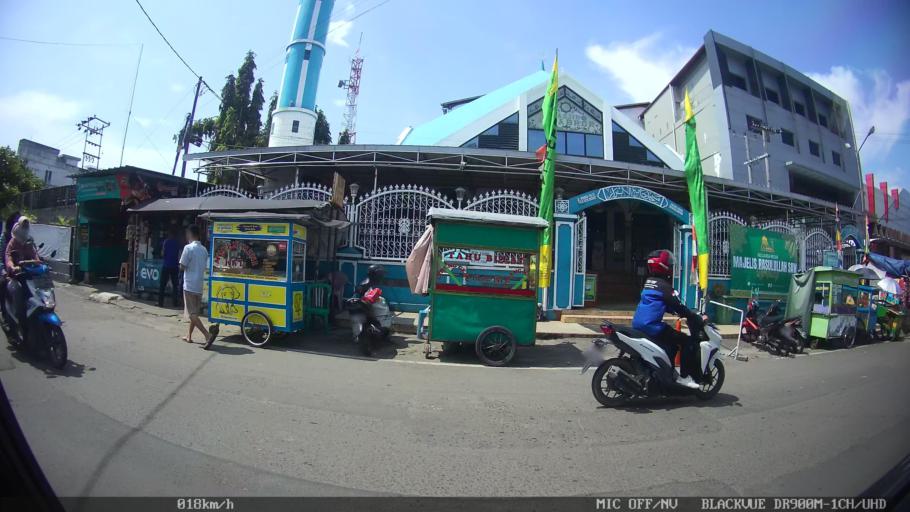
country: ID
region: Lampung
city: Bandarlampung
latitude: -5.4118
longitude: 105.2602
